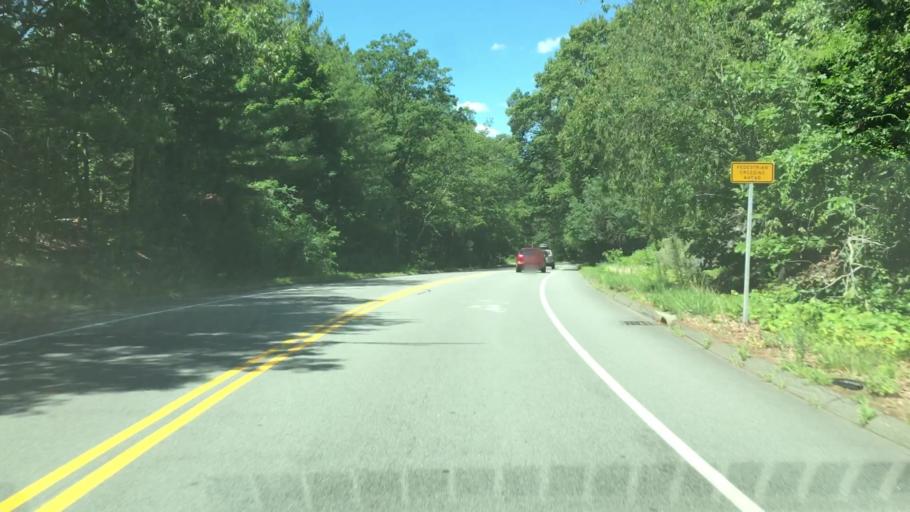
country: US
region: Massachusetts
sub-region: Middlesex County
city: Lexington
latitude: 42.4461
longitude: -71.2595
